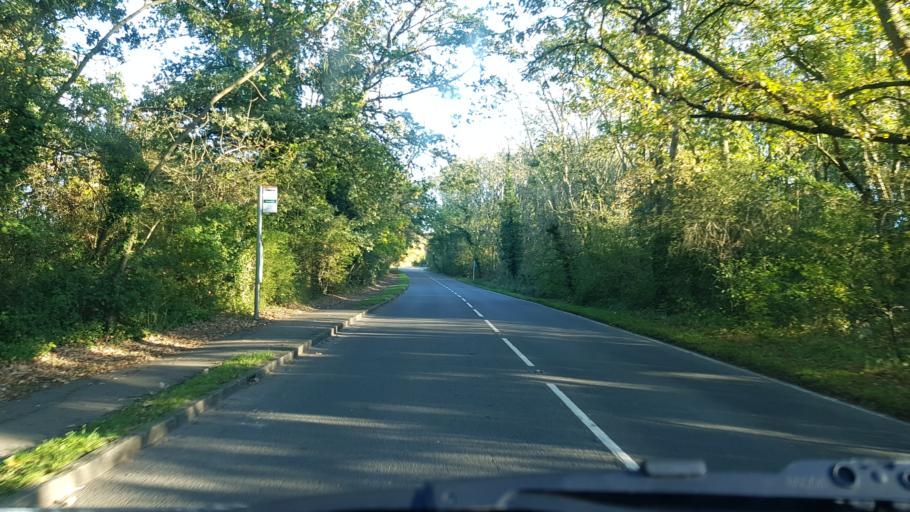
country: GB
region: England
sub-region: Surrey
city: Guildford
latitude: 51.2581
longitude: -0.6117
